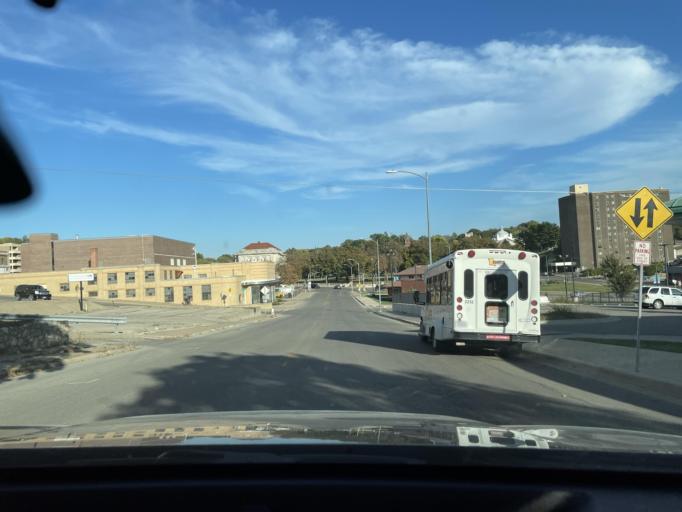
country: US
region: Missouri
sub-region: Buchanan County
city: Saint Joseph
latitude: 39.7682
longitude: -94.8504
